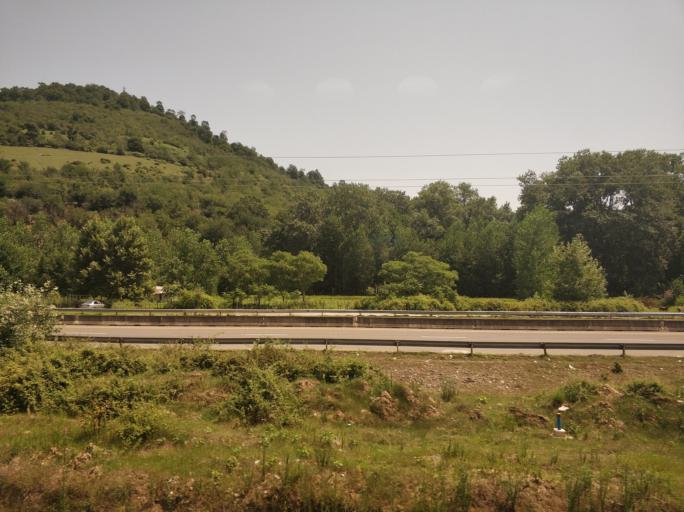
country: IR
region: Gilan
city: Pa'in-e Bazar-e Rudbar
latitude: 36.9624
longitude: 49.5532
